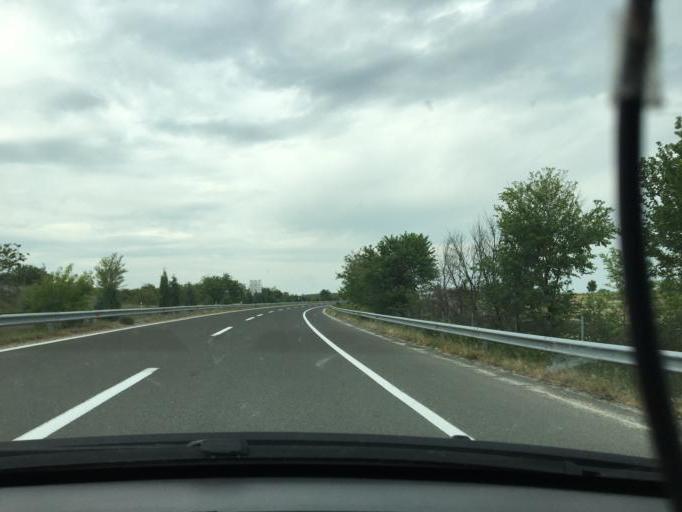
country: MK
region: Negotino
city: Negotino
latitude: 41.5063
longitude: 22.0877
